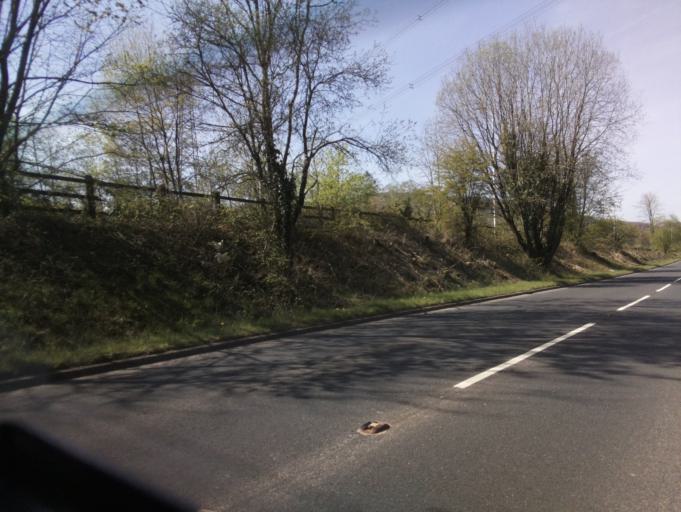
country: GB
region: Wales
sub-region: Rhondda Cynon Taf
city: Pontypridd
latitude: 51.6295
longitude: -3.3212
